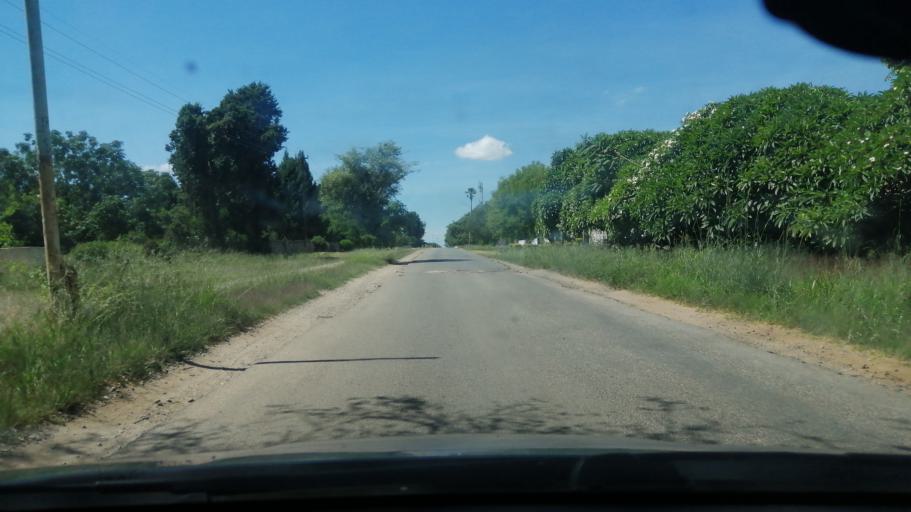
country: ZW
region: Harare
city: Epworth
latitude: -17.8234
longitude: 31.1261
